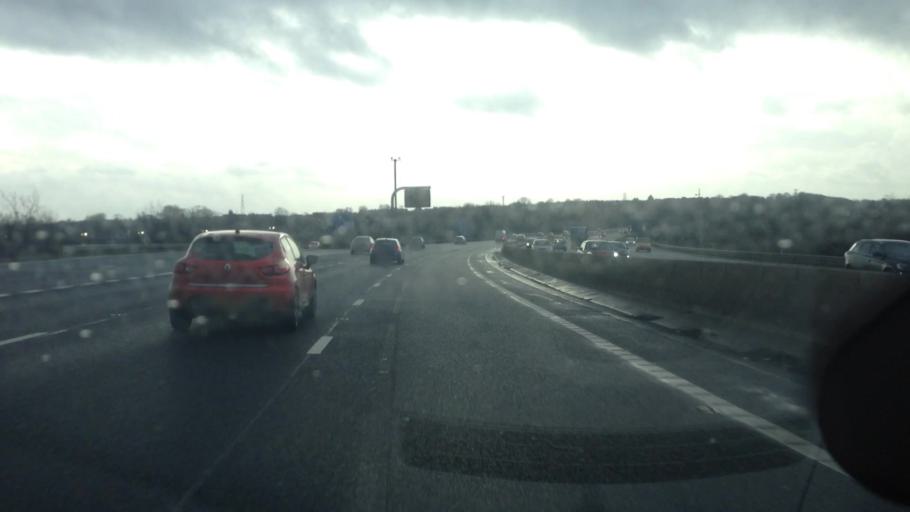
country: GB
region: England
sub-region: City and Borough of Wakefield
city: Crigglestone
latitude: 53.6544
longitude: -1.5280
